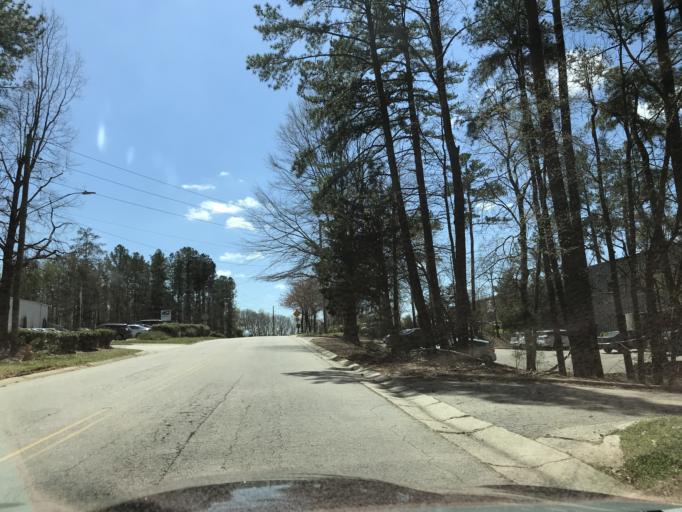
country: US
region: North Carolina
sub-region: Wake County
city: West Raleigh
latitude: 35.8694
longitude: -78.7154
